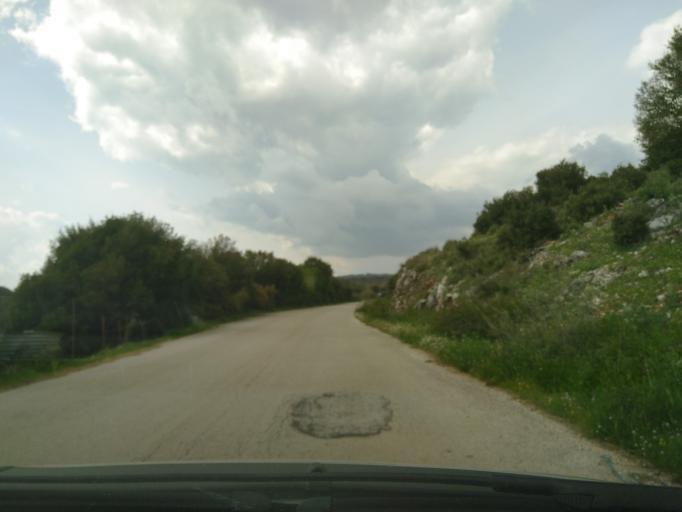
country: GR
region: Epirus
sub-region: Nomos Ioanninon
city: Asprangeloi
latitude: 39.7742
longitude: 20.6905
